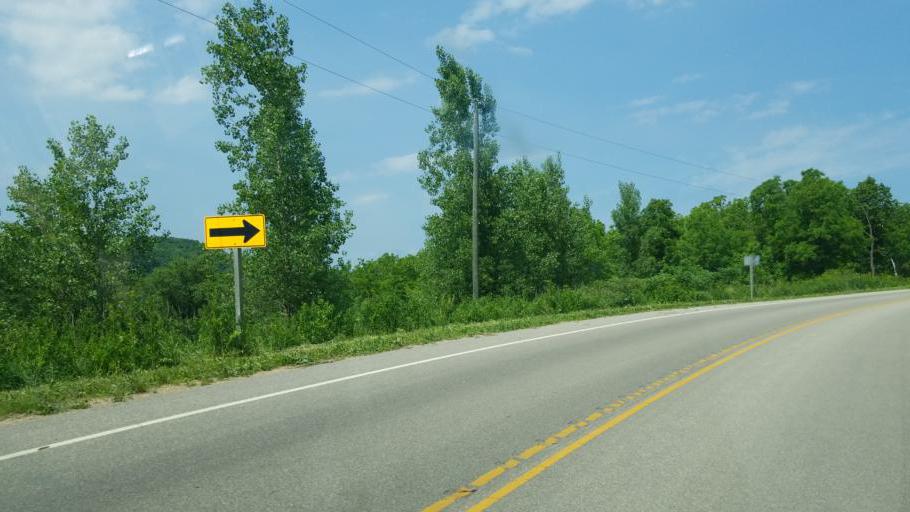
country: US
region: Wisconsin
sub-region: Vernon County
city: Viroqua
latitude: 43.4860
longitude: -90.6899
